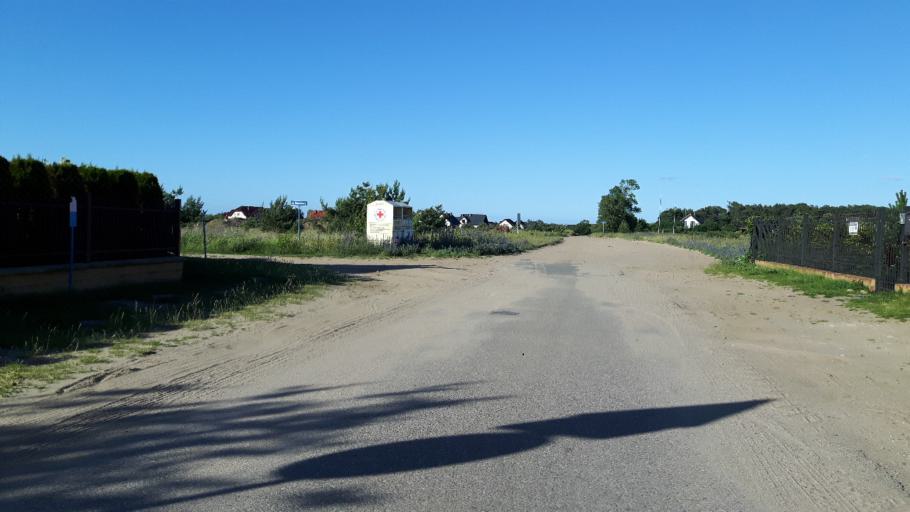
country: PL
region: Pomeranian Voivodeship
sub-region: Powiat pucki
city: Kosakowo
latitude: 54.6060
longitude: 18.4777
